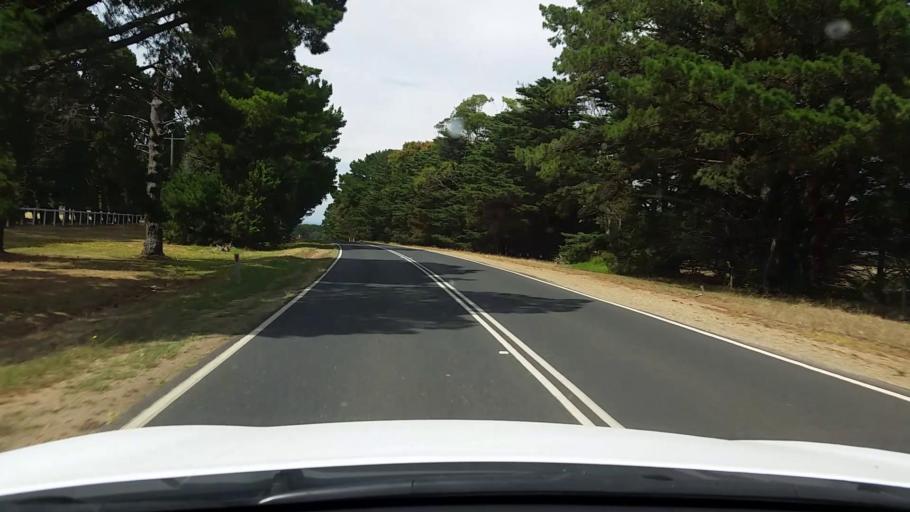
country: AU
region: Victoria
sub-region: Mornington Peninsula
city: Merricks
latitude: -38.4570
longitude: 145.0198
